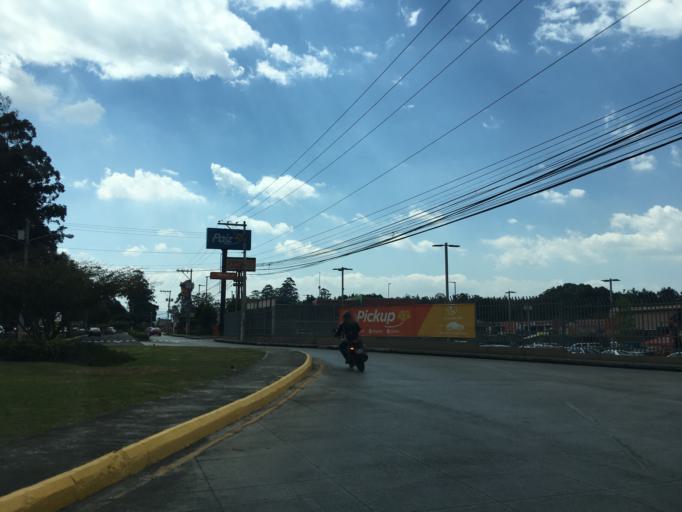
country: GT
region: Guatemala
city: Guatemala City
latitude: 14.6251
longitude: -90.4688
